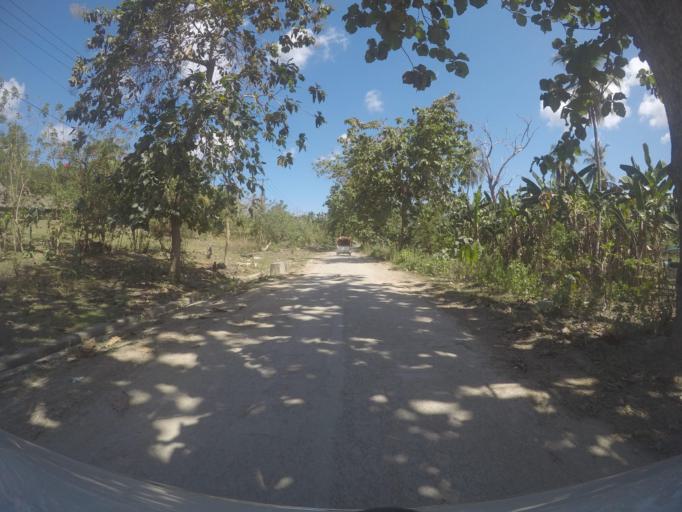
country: TL
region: Viqueque
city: Viqueque
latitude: -8.9154
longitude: 126.3974
